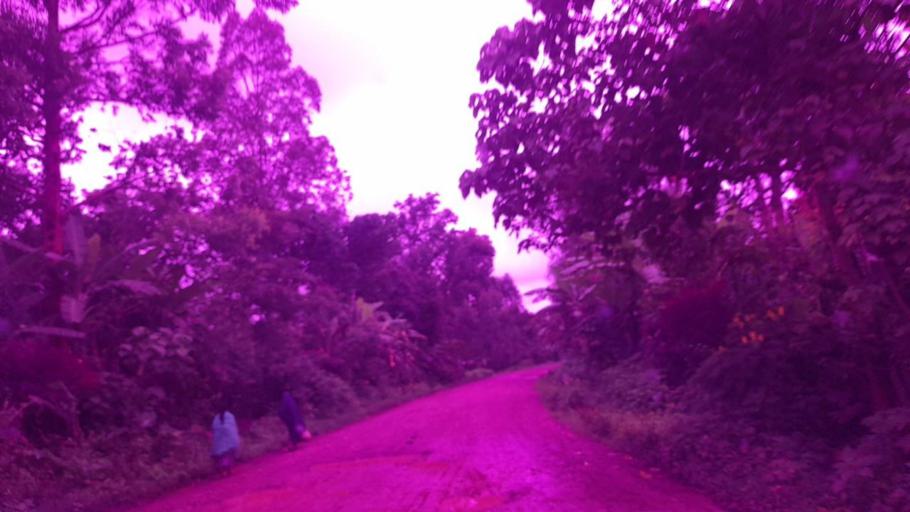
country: ET
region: Southern Nations, Nationalities, and People's Region
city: Bonga
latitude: 7.5749
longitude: 36.0252
